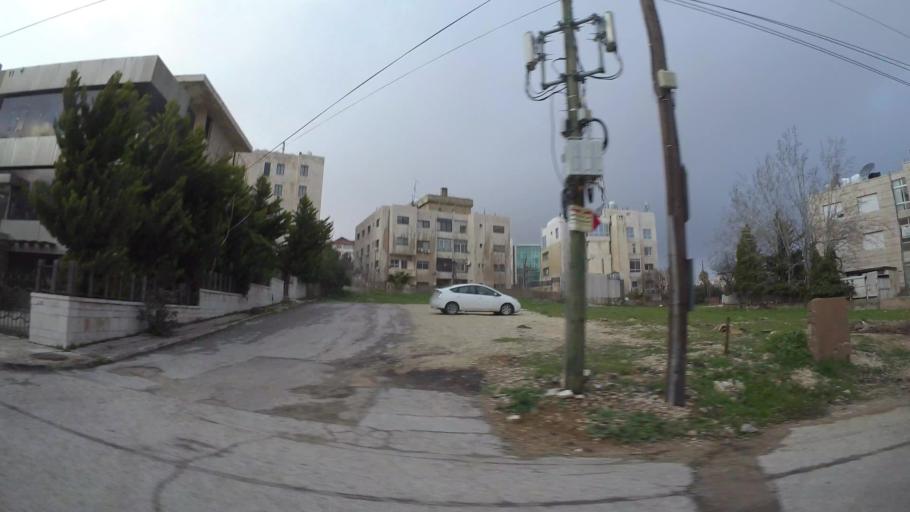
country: JO
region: Amman
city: Amman
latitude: 31.9623
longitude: 35.8836
